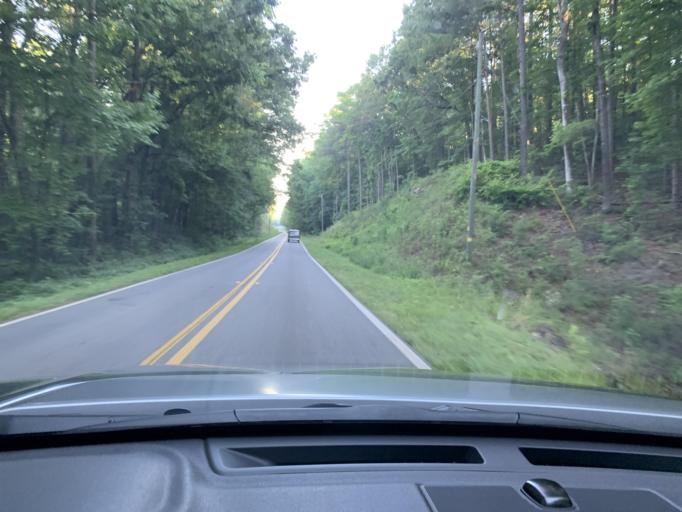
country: US
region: Georgia
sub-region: Bartow County
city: Rydal
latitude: 34.2725
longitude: -84.7304
